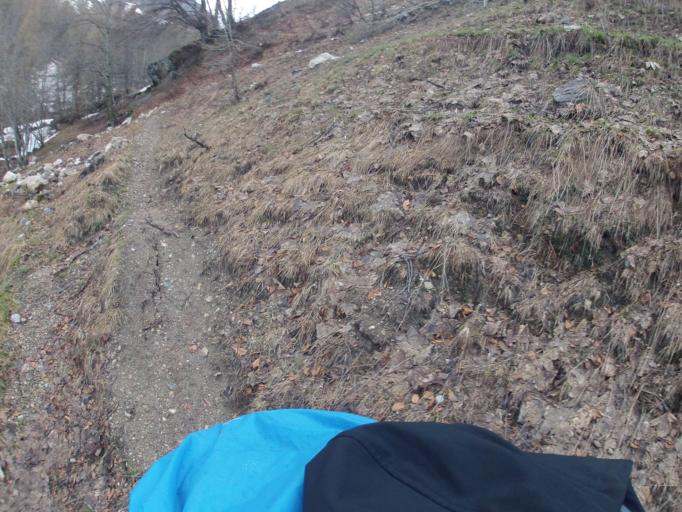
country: IT
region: Piedmont
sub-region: Provincia di Cuneo
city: Crissolo
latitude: 44.7005
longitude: 7.1294
